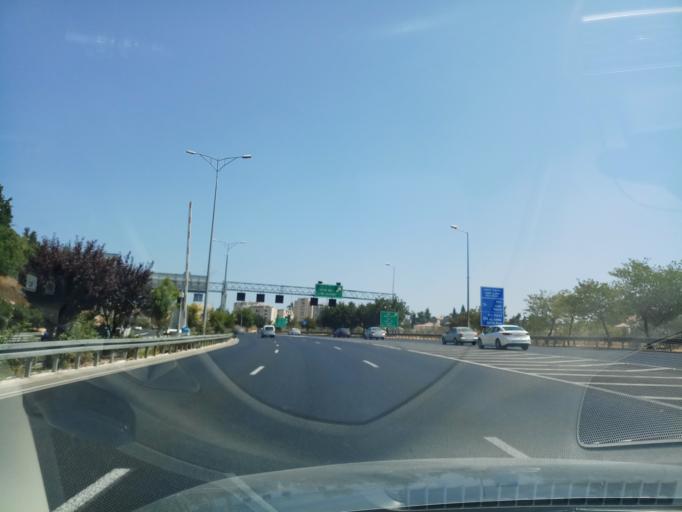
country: IL
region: Jerusalem
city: Jerusalem
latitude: 31.7592
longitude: 35.1936
